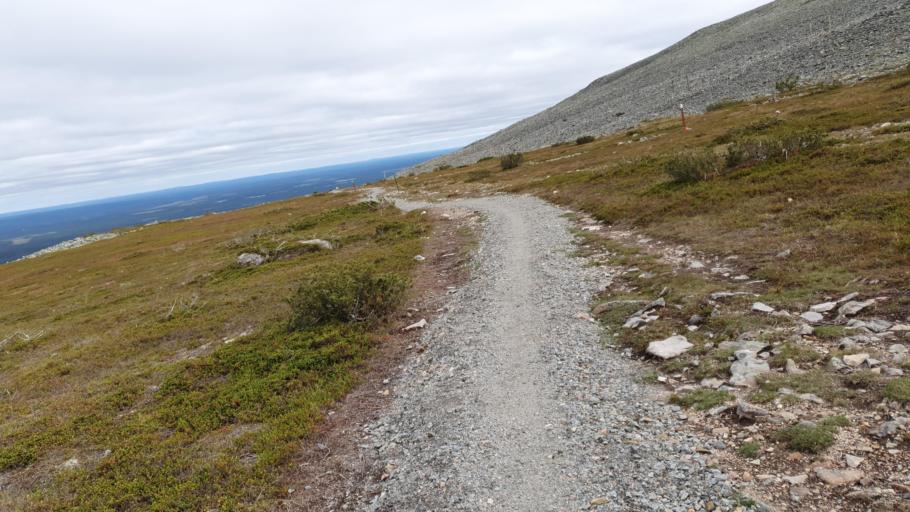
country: FI
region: Lapland
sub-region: Tunturi-Lappi
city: Kolari
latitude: 67.5696
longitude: 24.2333
